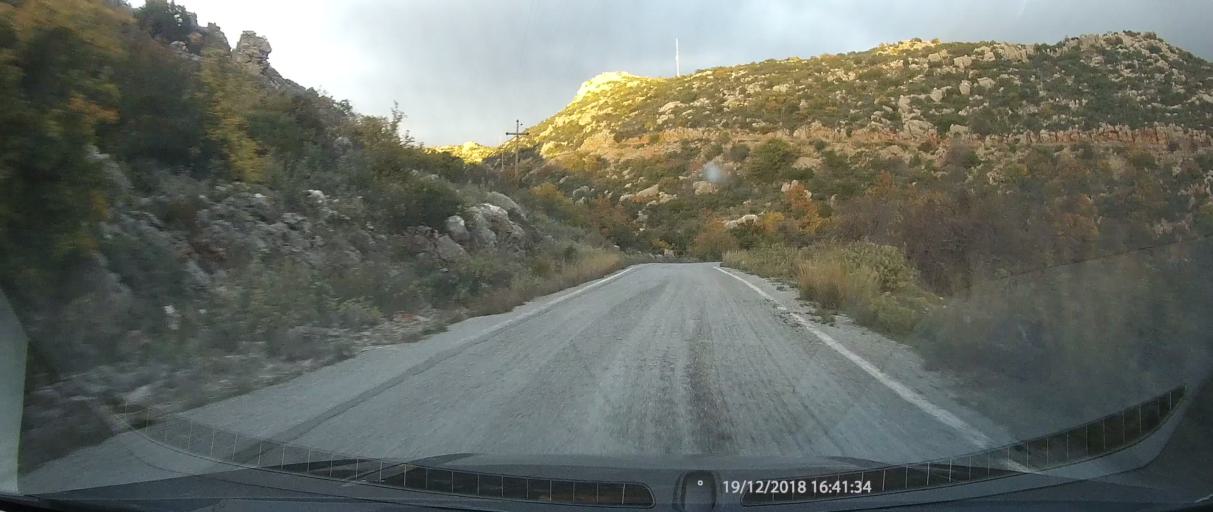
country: GR
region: Peloponnese
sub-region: Nomos Lakonias
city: Sykea
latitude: 36.9027
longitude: 22.9943
